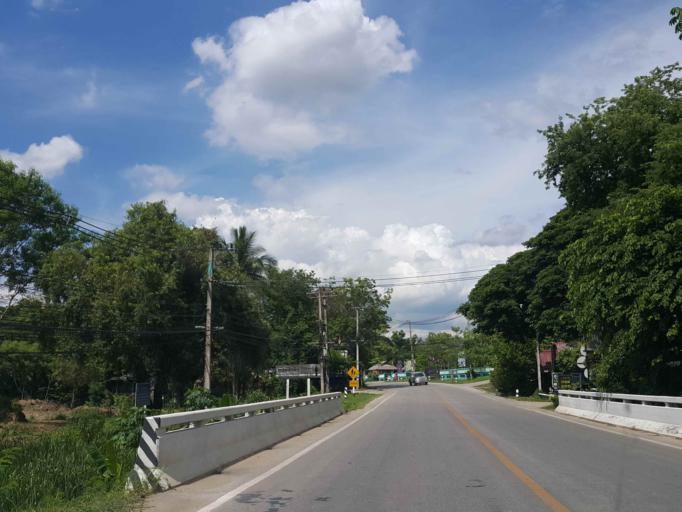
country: TH
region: Chiang Mai
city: Chiang Mai
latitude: 18.9153
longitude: 98.9071
